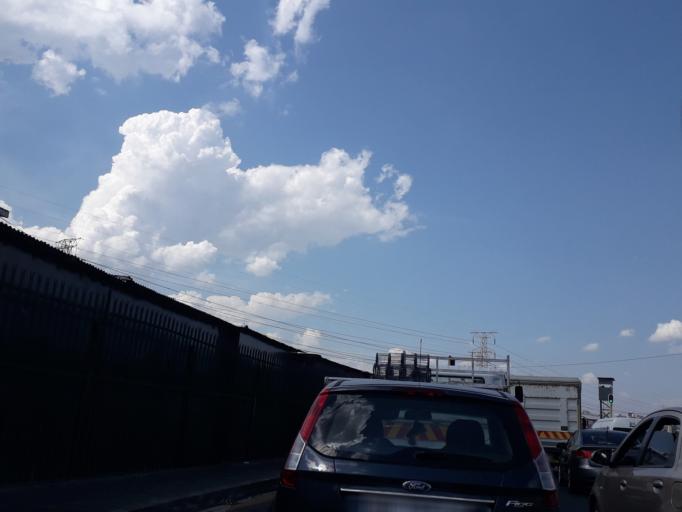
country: ZA
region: Gauteng
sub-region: City of Johannesburg Metropolitan Municipality
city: Johannesburg
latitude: -26.2116
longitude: 28.0180
